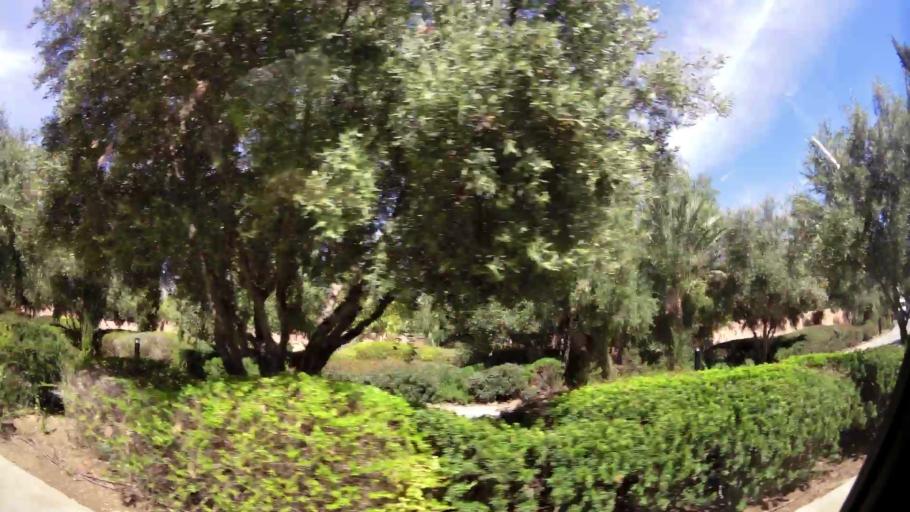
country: MA
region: Marrakech-Tensift-Al Haouz
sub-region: Marrakech
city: Marrakesh
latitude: 31.6043
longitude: -7.9544
